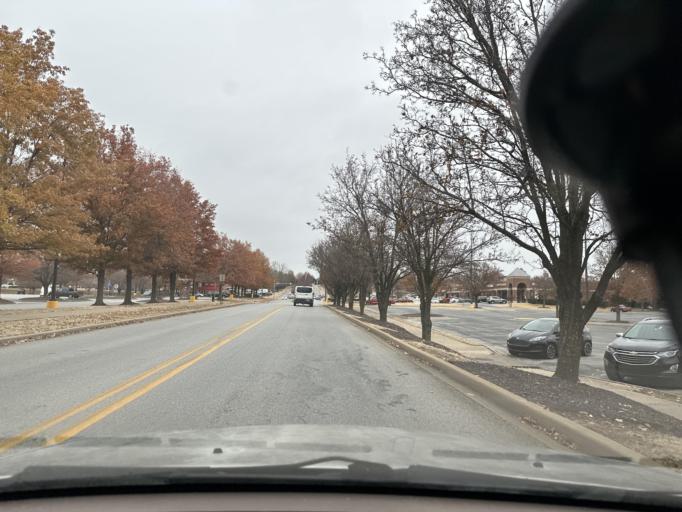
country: US
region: Arkansas
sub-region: Washington County
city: Johnson
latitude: 36.1217
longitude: -94.1498
